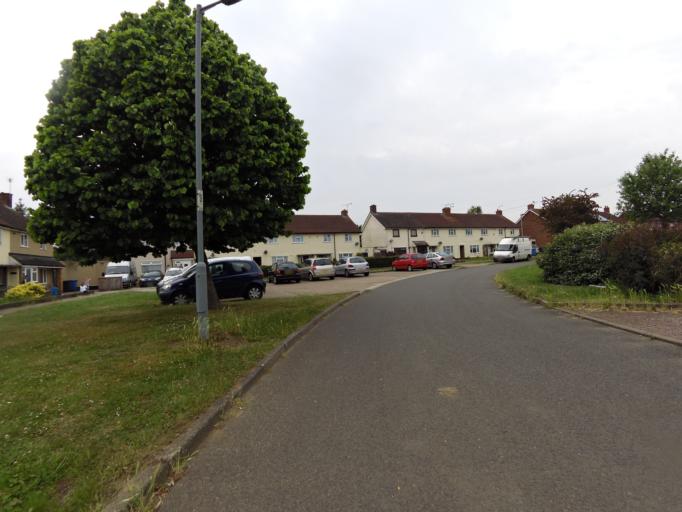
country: GB
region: England
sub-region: Suffolk
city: Ipswich
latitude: 52.0813
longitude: 1.1348
